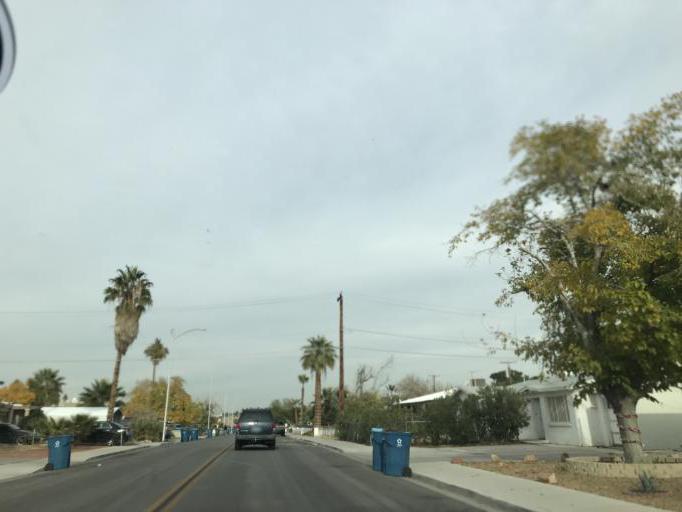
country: US
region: Nevada
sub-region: Clark County
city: Las Vegas
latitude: 36.1450
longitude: -115.1522
